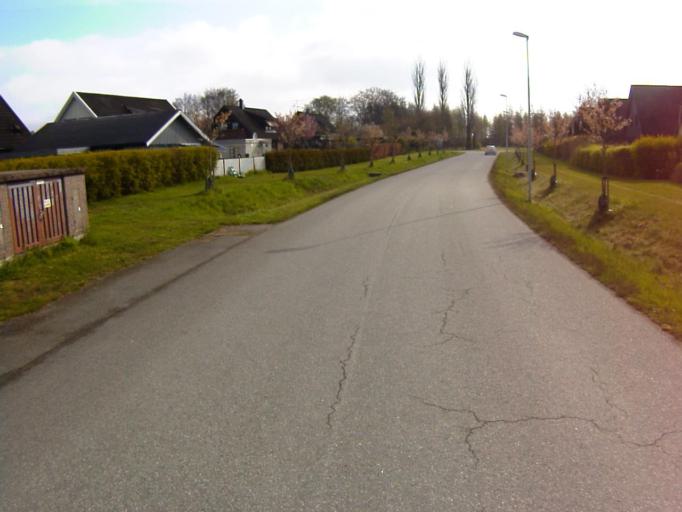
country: SE
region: Skane
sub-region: Kristianstads Kommun
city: Kristianstad
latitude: 56.0106
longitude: 14.1065
